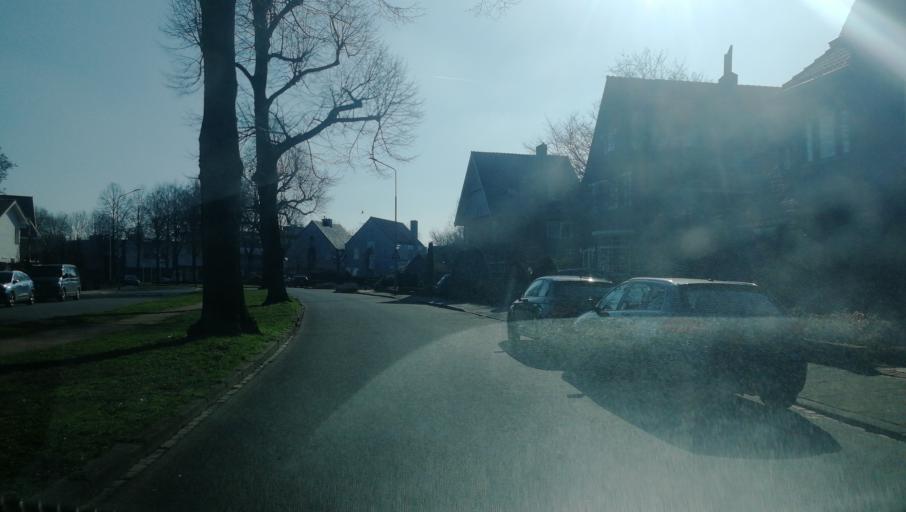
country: NL
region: Limburg
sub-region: Gemeente Venlo
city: Venlo
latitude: 51.3651
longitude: 6.1793
